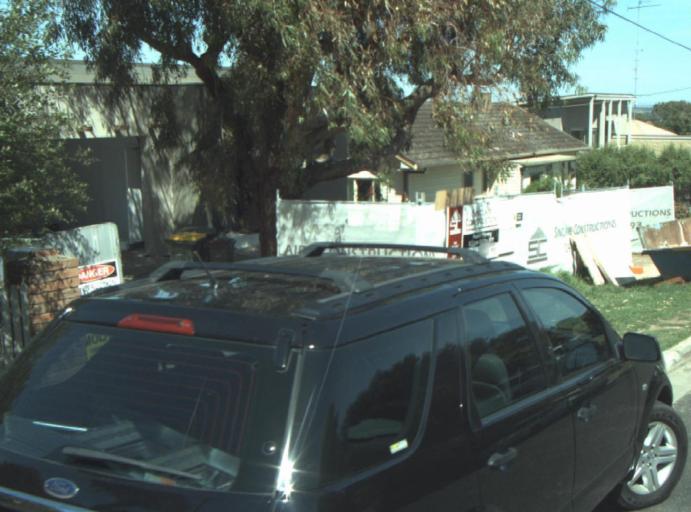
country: AU
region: Victoria
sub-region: Greater Geelong
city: Leopold
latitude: -38.2658
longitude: 144.5181
